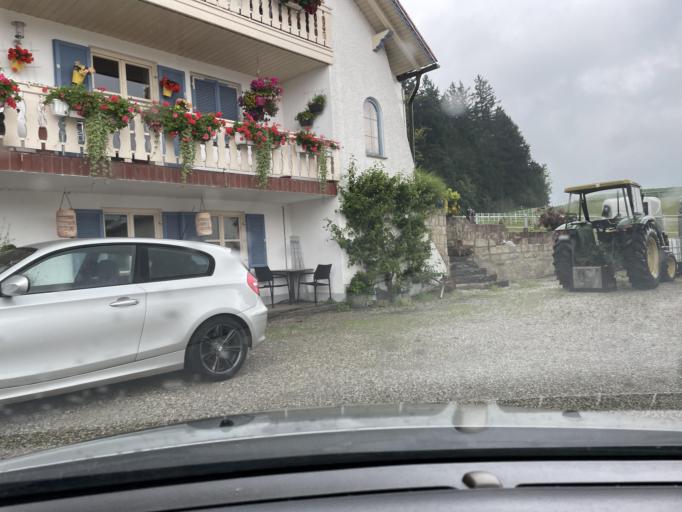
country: DE
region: Bavaria
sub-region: Lower Bavaria
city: Vilsheim
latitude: 48.4308
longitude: 12.1137
